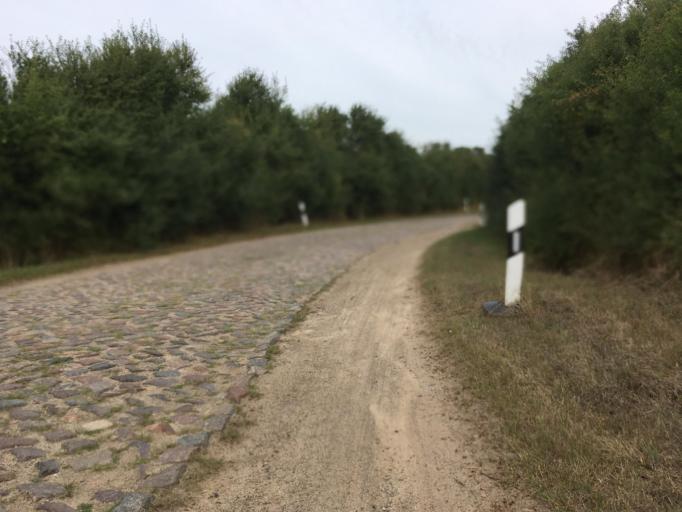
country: DE
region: Brandenburg
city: Gerswalde
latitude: 53.1285
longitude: 13.7197
